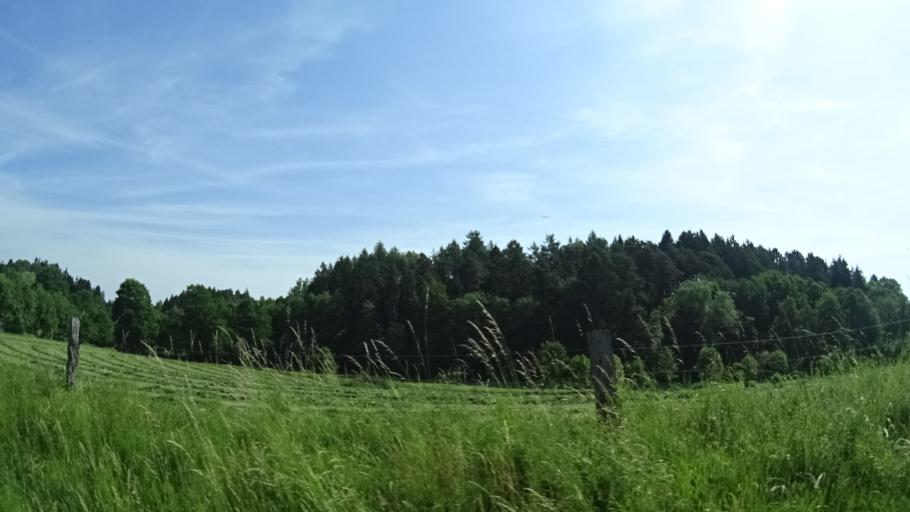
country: DE
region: Hesse
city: Rosenthal
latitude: 50.9289
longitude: 8.8408
